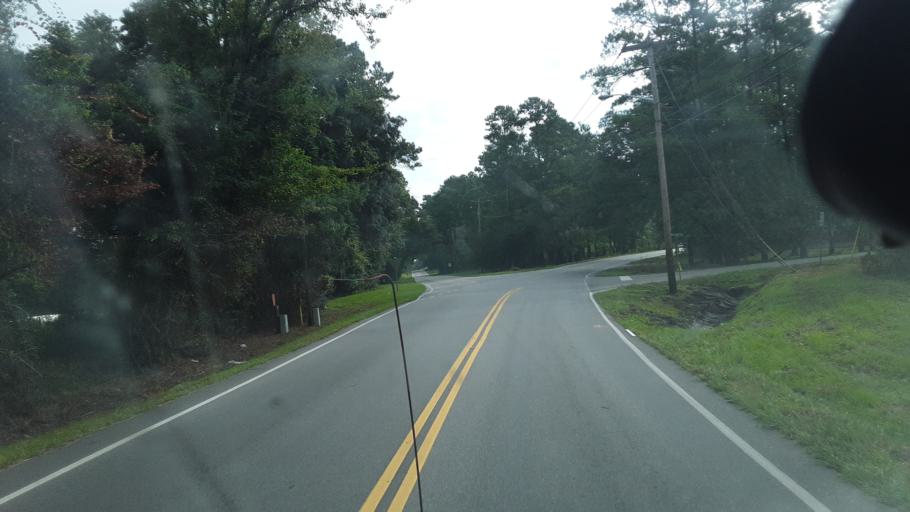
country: US
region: South Carolina
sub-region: Horry County
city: Conway
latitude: 33.8225
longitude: -79.0819
